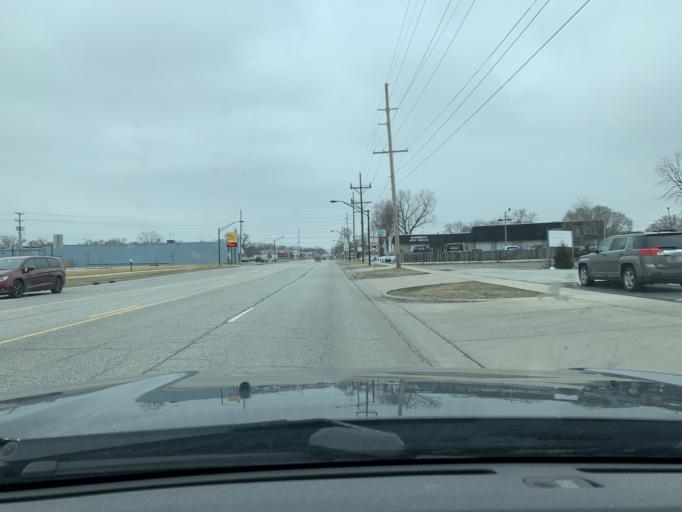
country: US
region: Indiana
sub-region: Lake County
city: Highland
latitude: 41.5677
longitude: -87.4617
